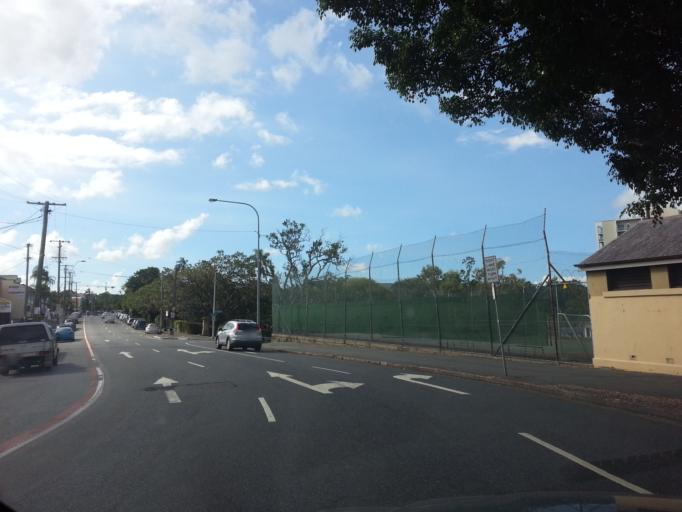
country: AU
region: Queensland
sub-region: Brisbane
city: Spring Hill
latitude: -27.4641
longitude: 153.0143
